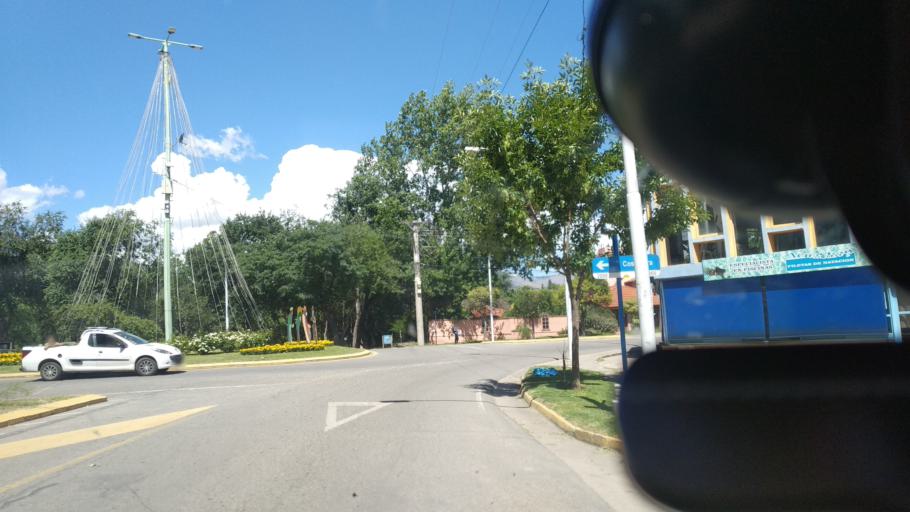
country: AR
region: Cordoba
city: Mina Clavero
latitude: -31.7202
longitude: -65.0073
